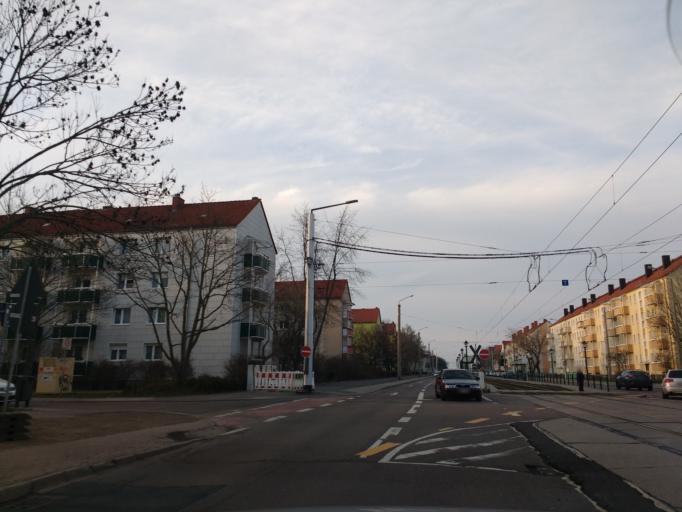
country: DE
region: Saxony-Anhalt
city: Halle Neustadt
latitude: 51.4521
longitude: 11.9611
